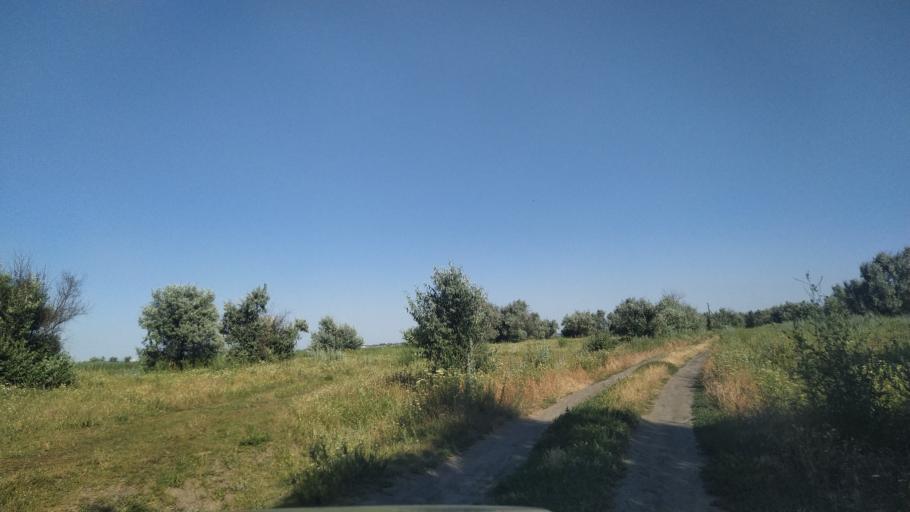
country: RU
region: Rostov
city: Kuleshovka
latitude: 47.1360
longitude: 39.6400
